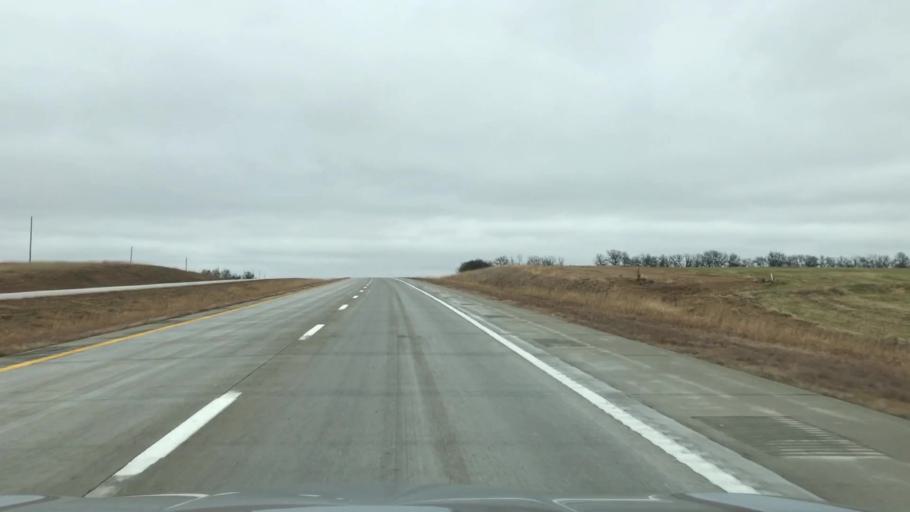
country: US
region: Missouri
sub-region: Livingston County
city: Chillicothe
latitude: 39.7347
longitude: -93.7691
